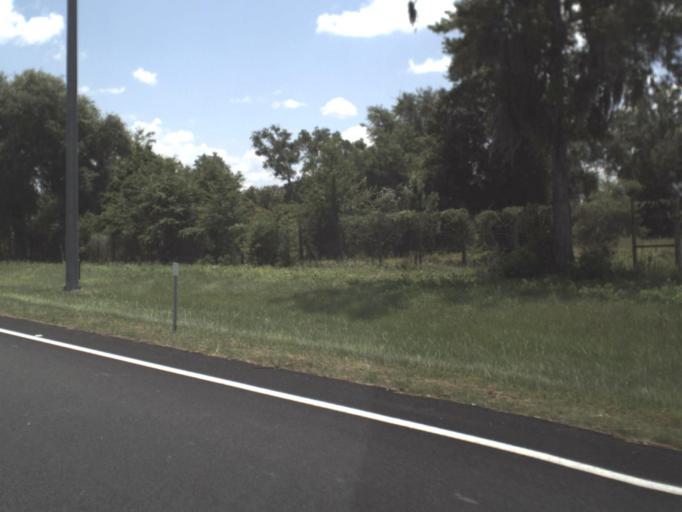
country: US
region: Florida
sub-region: Madison County
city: Madison
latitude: 30.3947
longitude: -83.3507
